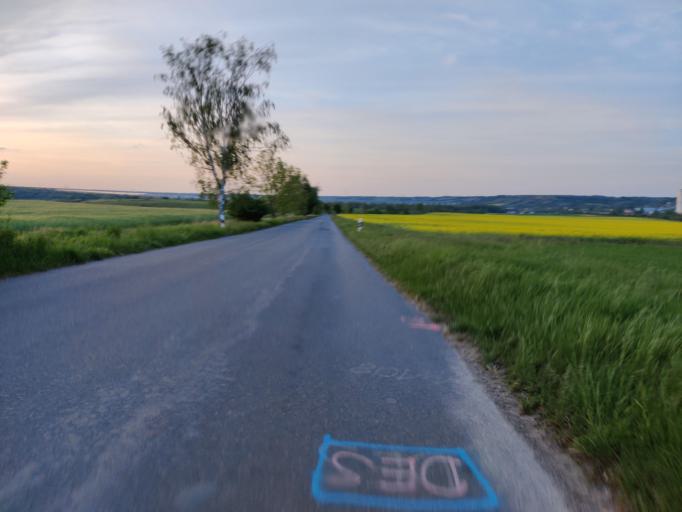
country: DE
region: Saxony-Anhalt
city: Karsdorf
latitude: 51.2546
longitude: 11.6443
